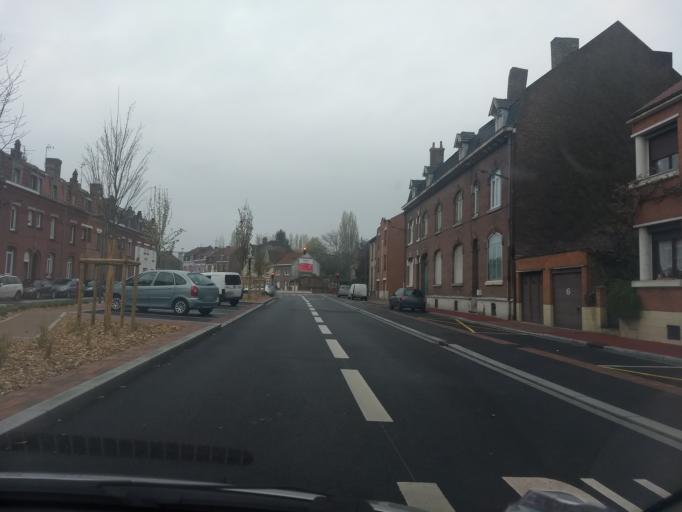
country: FR
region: Nord-Pas-de-Calais
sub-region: Departement du Nord
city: Douai
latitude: 50.3686
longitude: 3.0641
